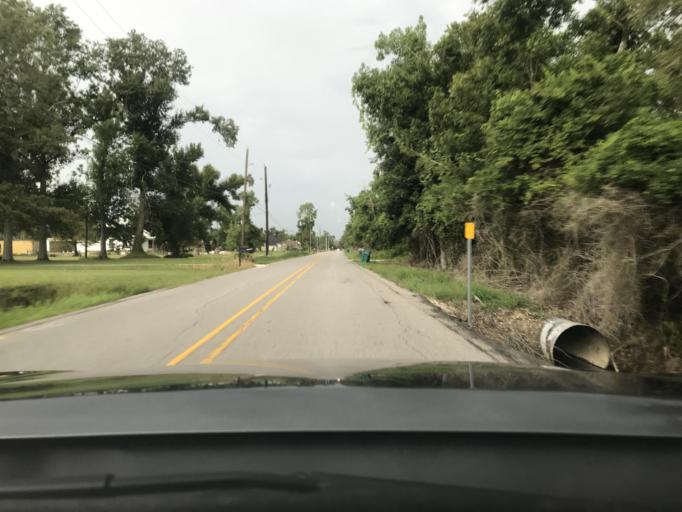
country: US
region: Louisiana
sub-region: Calcasieu Parish
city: Westlake
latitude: 30.2570
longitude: -93.2333
